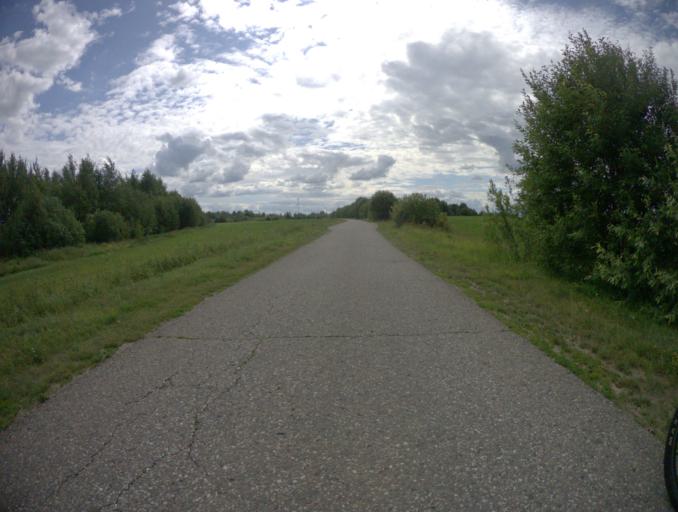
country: RU
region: Vladimir
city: Orgtrud
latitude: 56.3178
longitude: 40.6193
